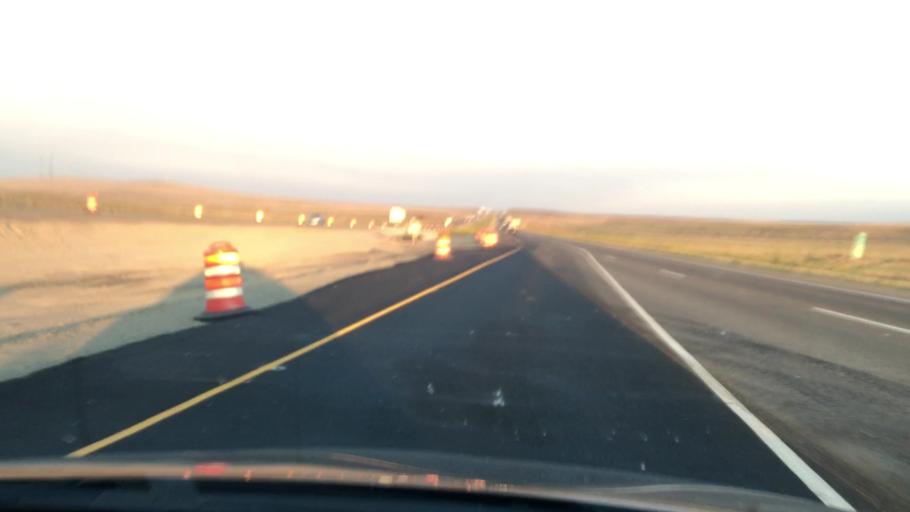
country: US
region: Idaho
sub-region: Minidoka County
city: Rupert
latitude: 42.5600
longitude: -113.4993
